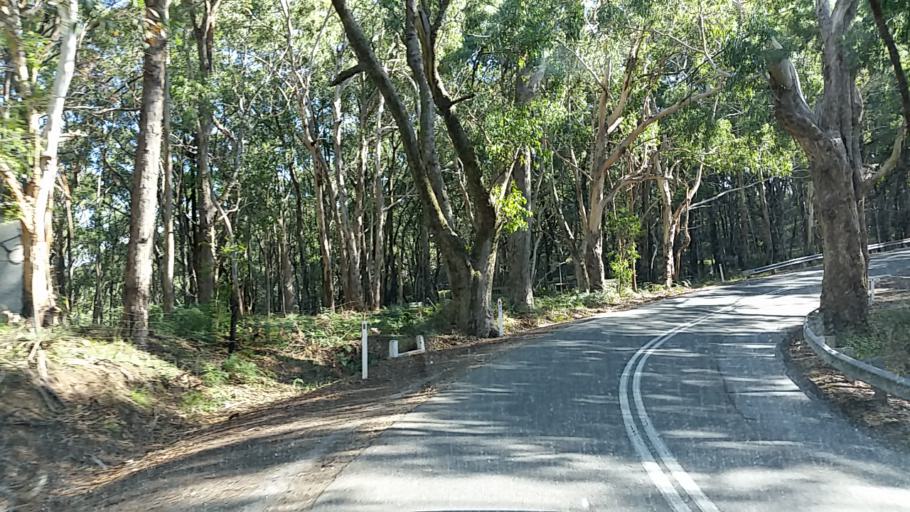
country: AU
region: South Australia
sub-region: Adelaide Hills
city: Crafers
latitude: -34.9613
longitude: 138.7139
